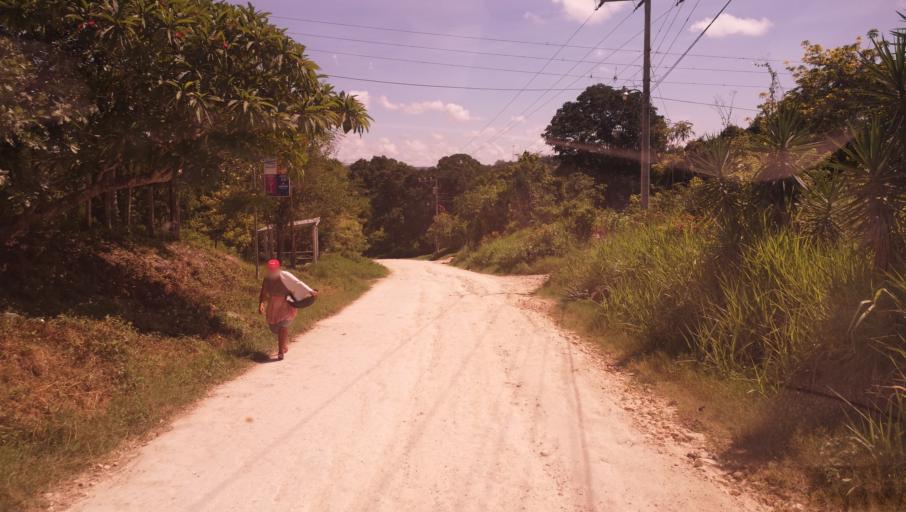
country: GT
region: Peten
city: Melchor de Mencos
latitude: 16.9712
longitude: -89.2651
